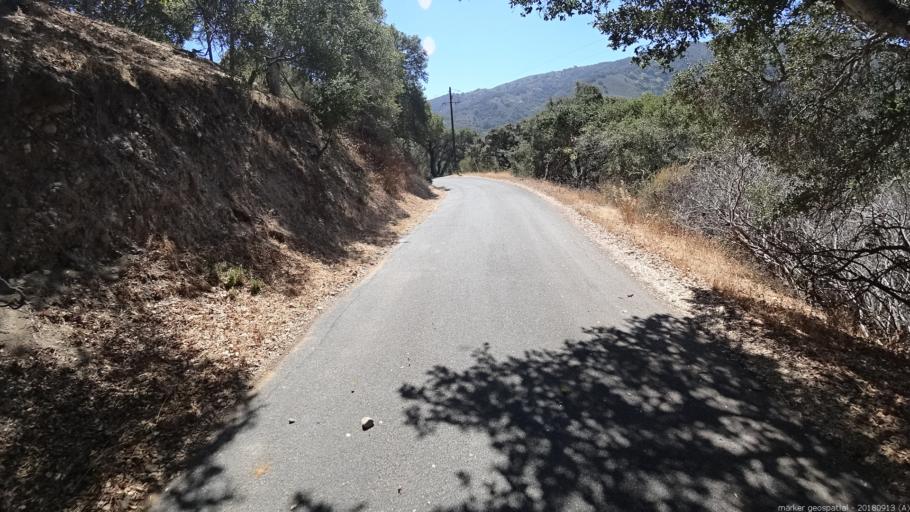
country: US
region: California
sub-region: Monterey County
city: Carmel Valley Village
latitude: 36.5131
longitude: -121.7693
